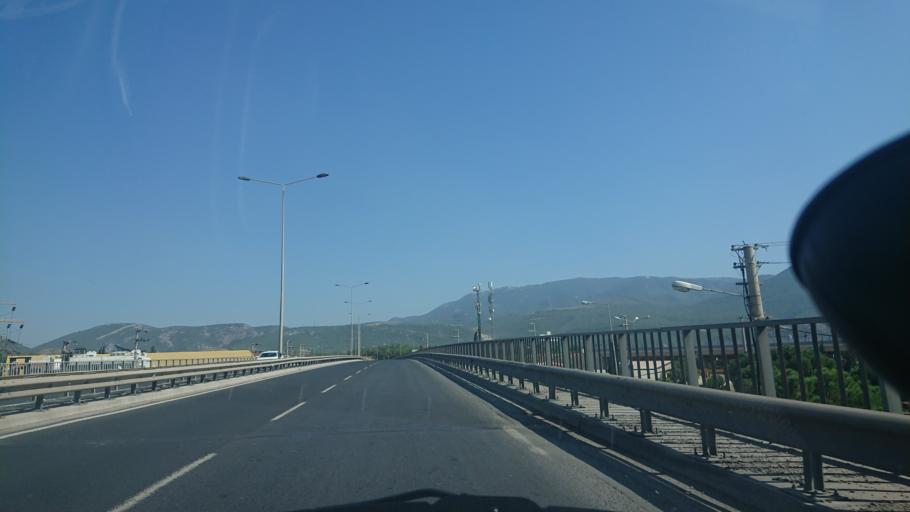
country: TR
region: Izmir
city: Bornova
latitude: 38.4527
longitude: 27.2648
